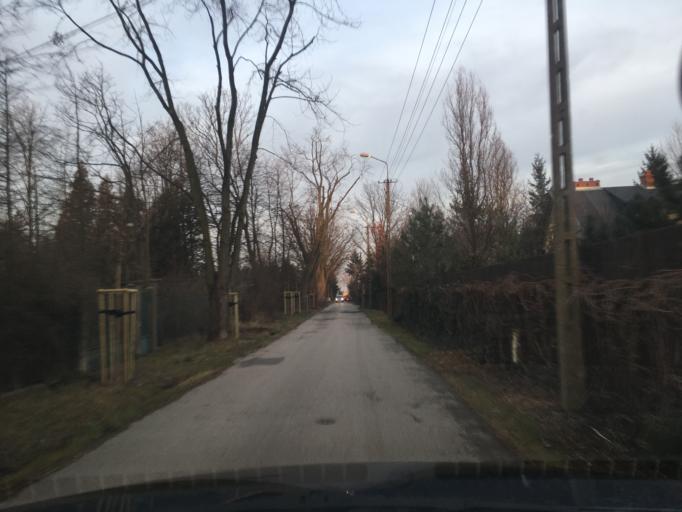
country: PL
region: Masovian Voivodeship
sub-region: Powiat piaseczynski
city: Lesznowola
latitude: 52.0360
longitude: 20.9580
